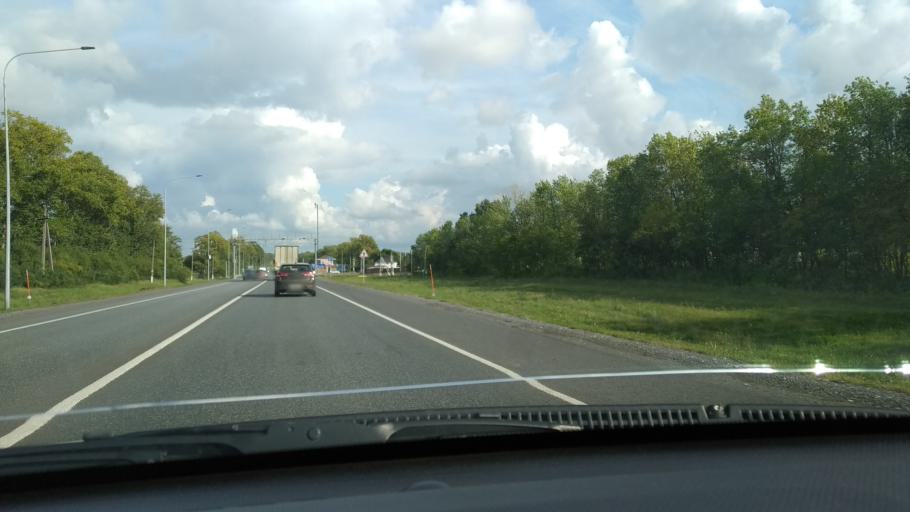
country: RU
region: Tatarstan
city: Stolbishchi
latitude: 55.6572
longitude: 49.3083
